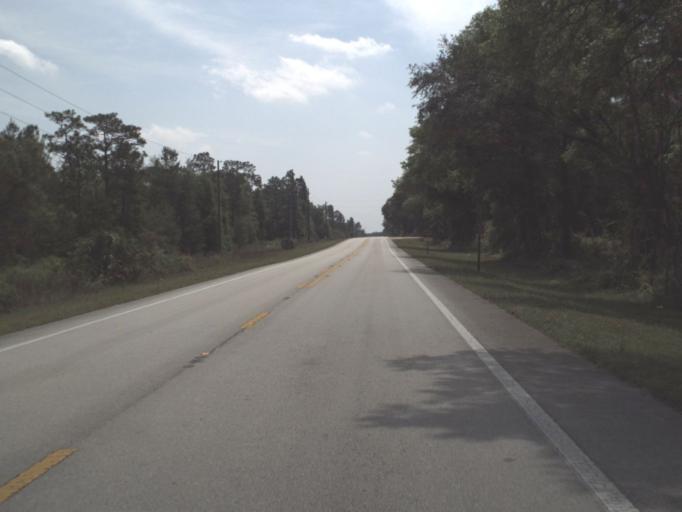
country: US
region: Florida
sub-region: Putnam County
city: Crescent City
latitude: 29.3388
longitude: -81.7277
